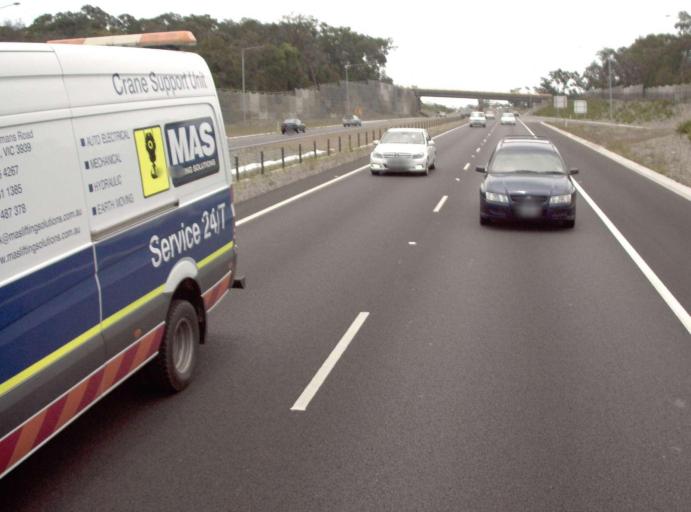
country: AU
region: Victoria
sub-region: Frankston
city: Langwarrin
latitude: -38.1798
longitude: 145.1602
